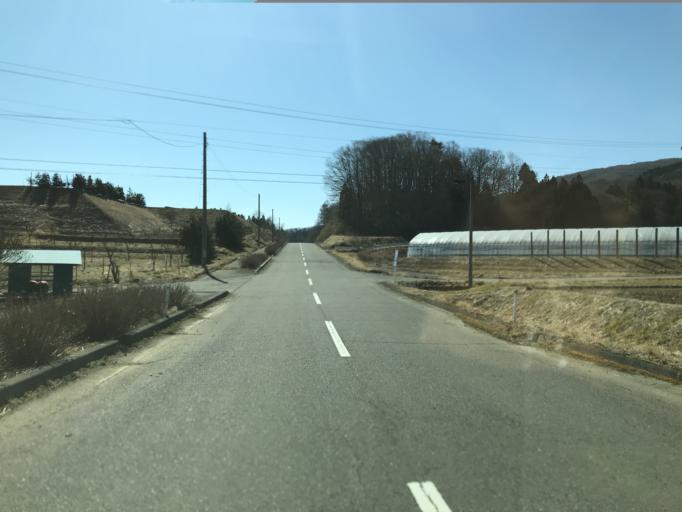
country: JP
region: Fukushima
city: Funehikimachi-funehiki
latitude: 37.3662
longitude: 140.5955
